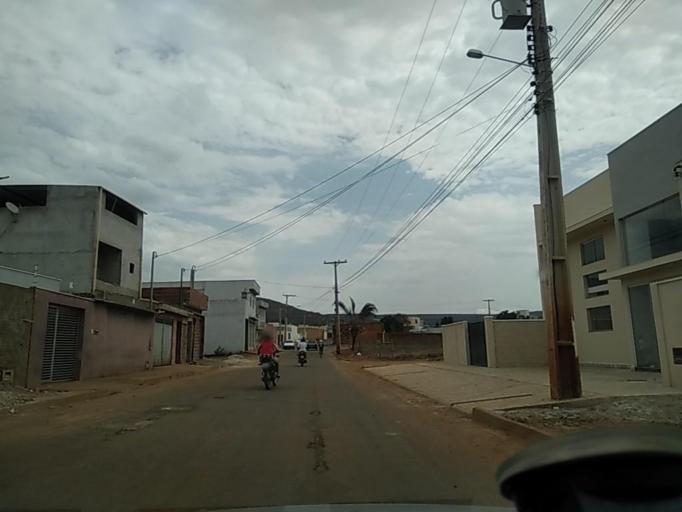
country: BR
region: Bahia
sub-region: Caetite
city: Caetite
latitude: -14.0607
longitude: -42.4738
